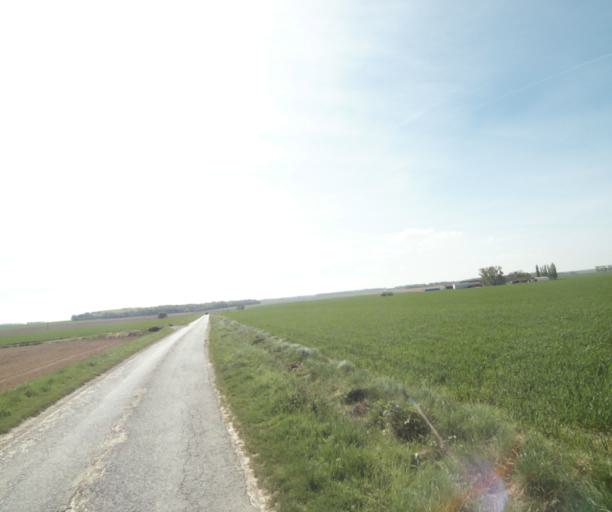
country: FR
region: Ile-de-France
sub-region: Departement de Seine-et-Marne
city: Nangis
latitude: 48.5508
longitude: 3.0321
